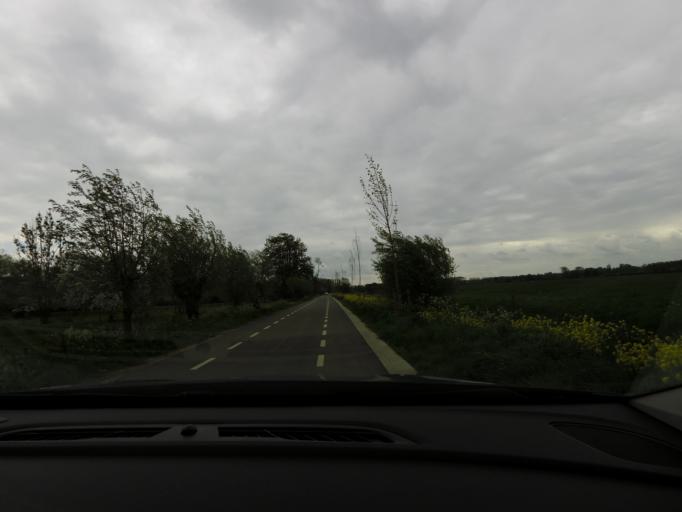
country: NL
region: North Brabant
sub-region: Gemeente Woudrichem
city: Woudrichem
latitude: 51.8566
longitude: 5.0348
